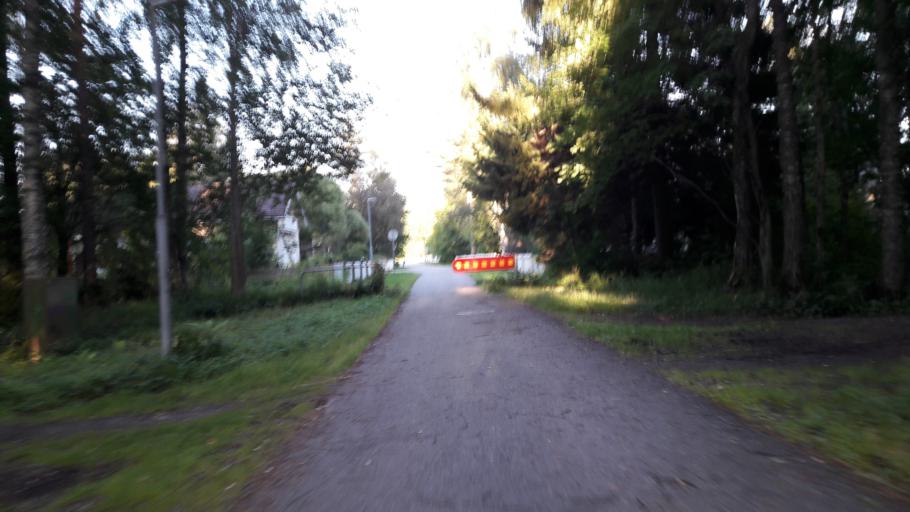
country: FI
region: North Karelia
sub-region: Joensuu
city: Joensuu
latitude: 62.6140
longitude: 29.7096
